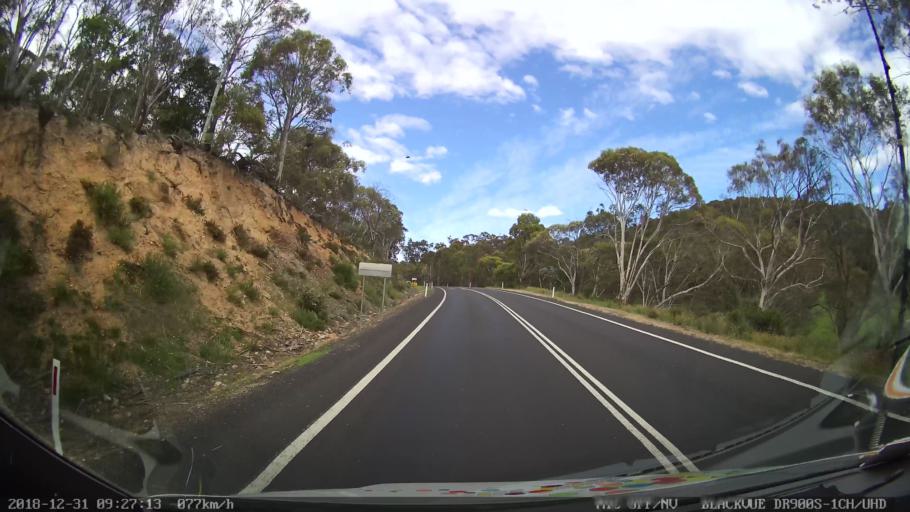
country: AU
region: New South Wales
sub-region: Snowy River
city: Jindabyne
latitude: -36.4548
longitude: 148.4875
